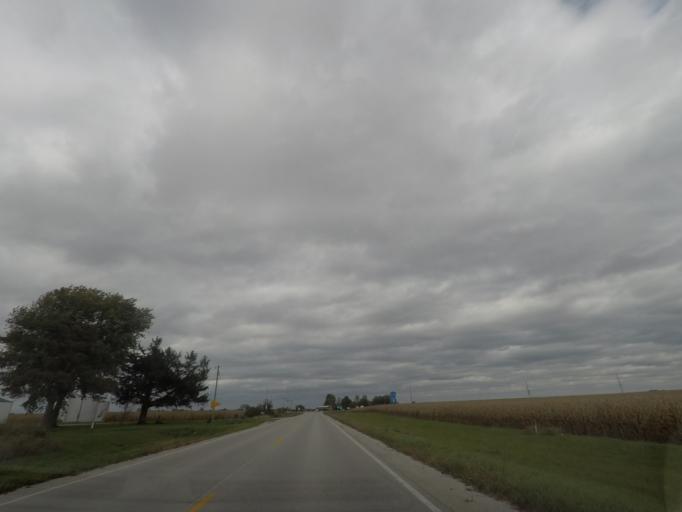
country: US
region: Iowa
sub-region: Story County
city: Huxley
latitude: 41.8756
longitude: -93.5314
